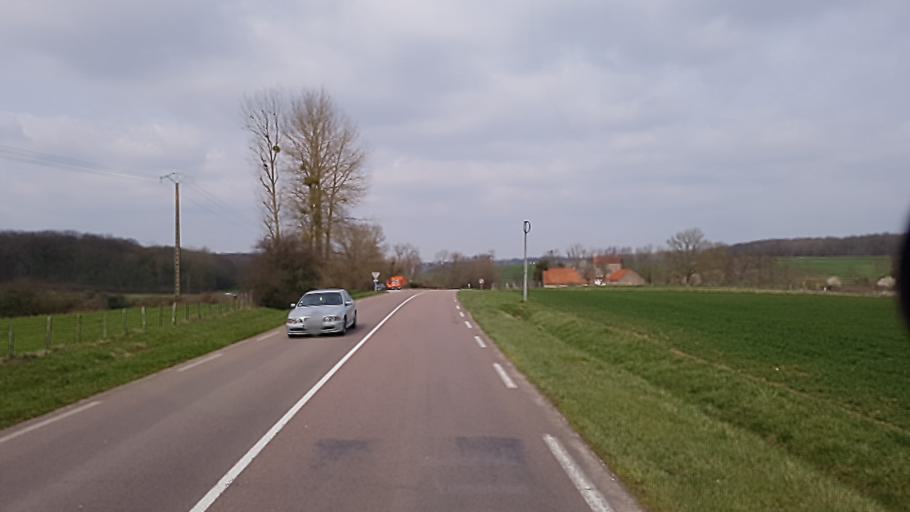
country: FR
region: Franche-Comte
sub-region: Departement du Jura
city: Champvans
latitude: 47.1433
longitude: 5.4223
